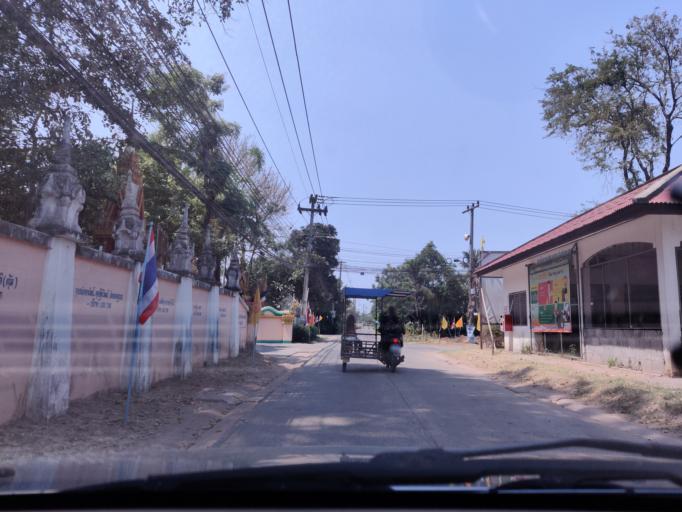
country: TH
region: Sisaket
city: Si Sa Ket
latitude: 15.1050
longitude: 104.3518
